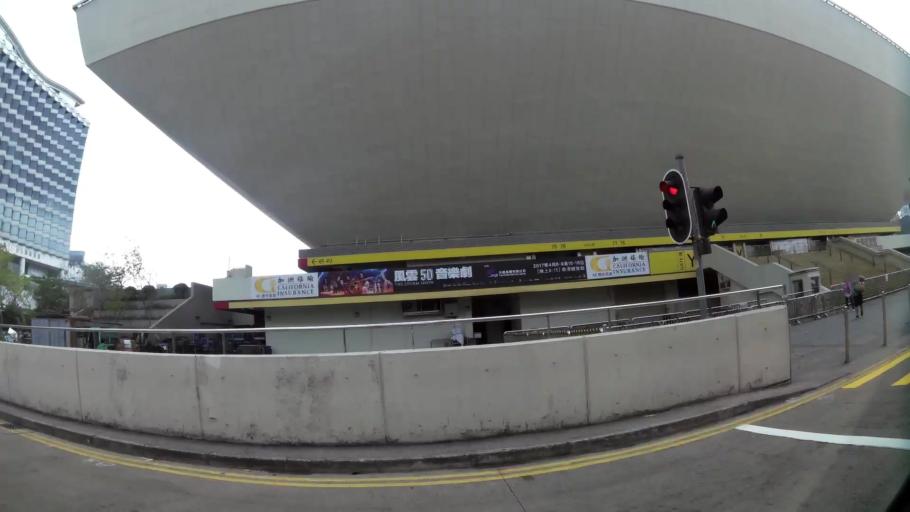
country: HK
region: Kowloon City
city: Kowloon
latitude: 22.3020
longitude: 114.1823
